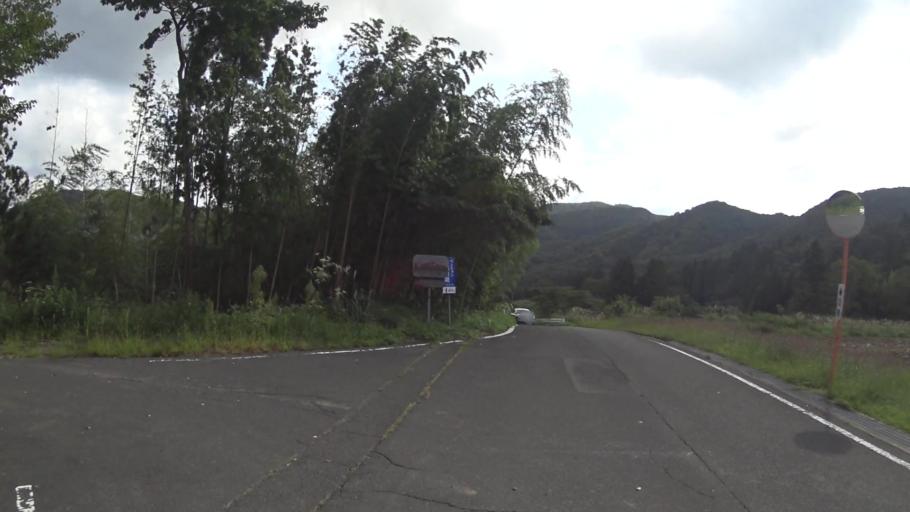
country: JP
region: Kyoto
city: Miyazu
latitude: 35.6554
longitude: 135.1839
